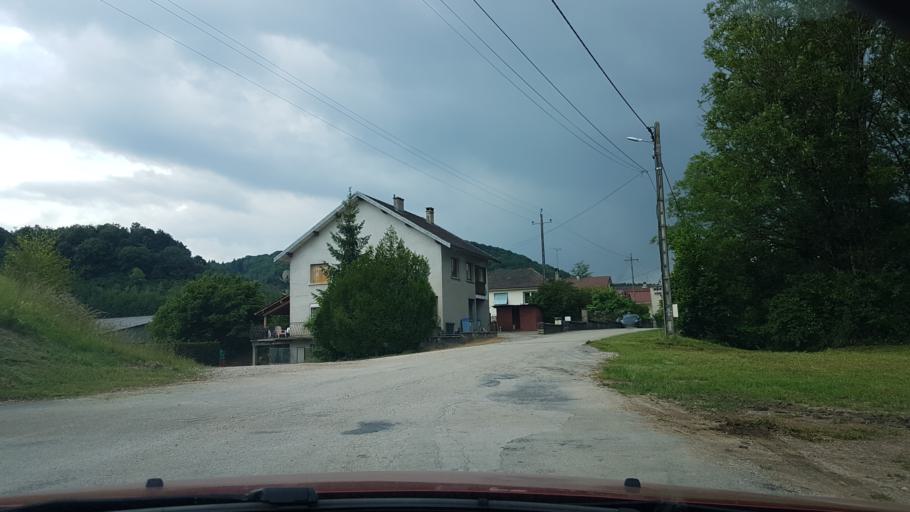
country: FR
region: Franche-Comte
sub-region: Departement du Jura
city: Orgelet
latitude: 46.5543
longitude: 5.6735
